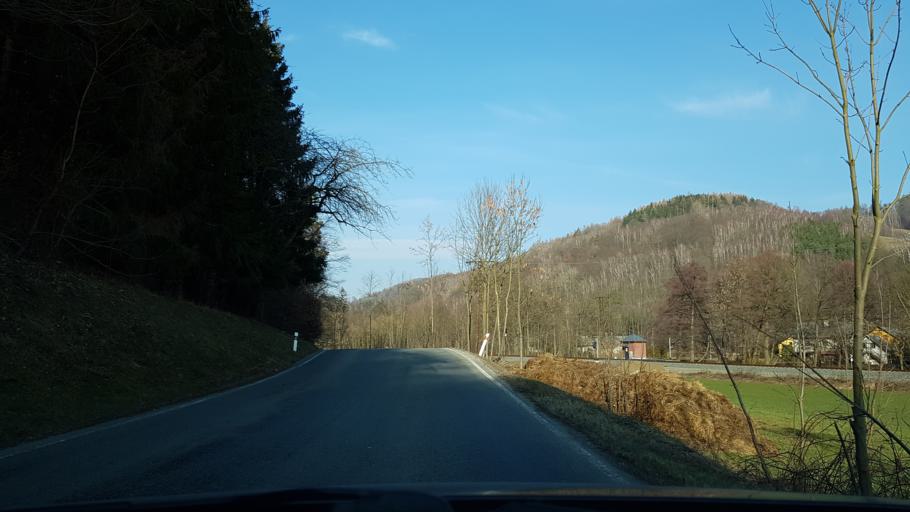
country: CZ
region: Olomoucky
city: Dolni Bohdikov
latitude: 50.0150
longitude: 16.8971
